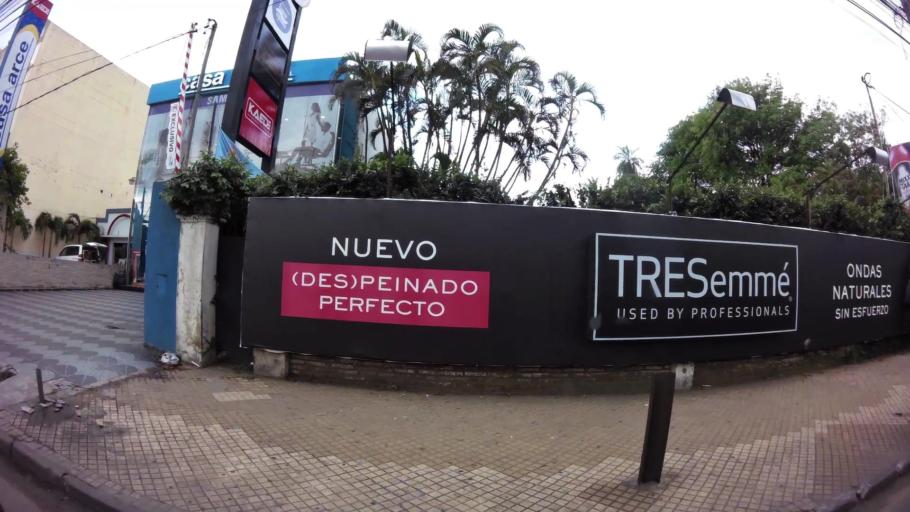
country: PY
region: Asuncion
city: Asuncion
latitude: -25.2853
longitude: -57.5770
